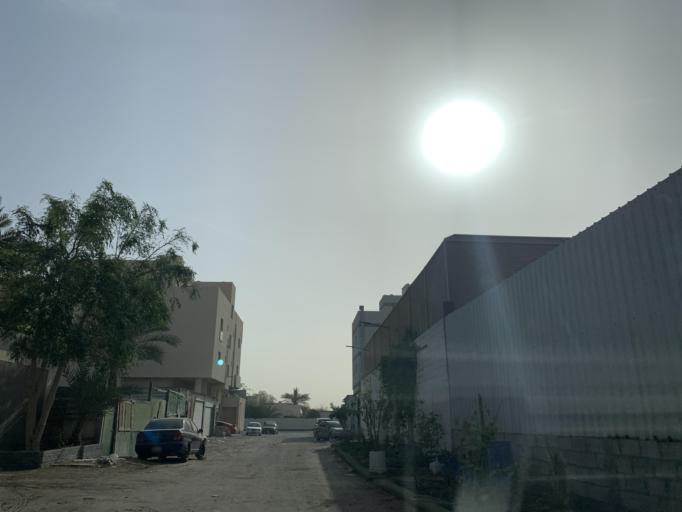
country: BH
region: Northern
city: Madinat `Isa
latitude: 26.1826
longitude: 50.5586
